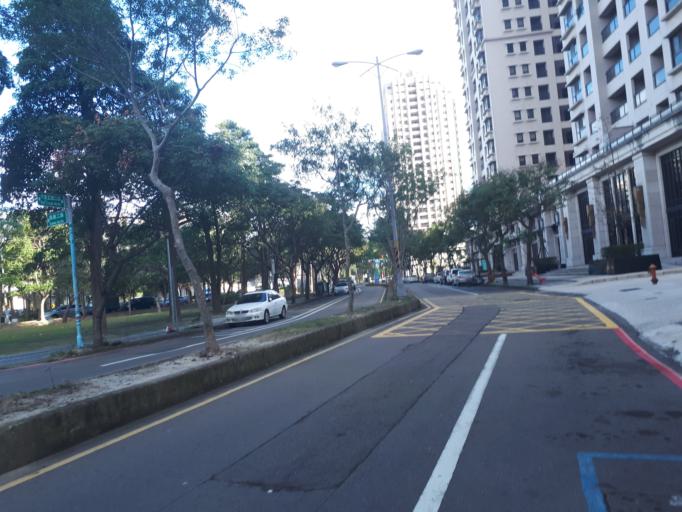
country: TW
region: Taiwan
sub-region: Hsinchu
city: Zhubei
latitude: 24.8022
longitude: 121.0370
